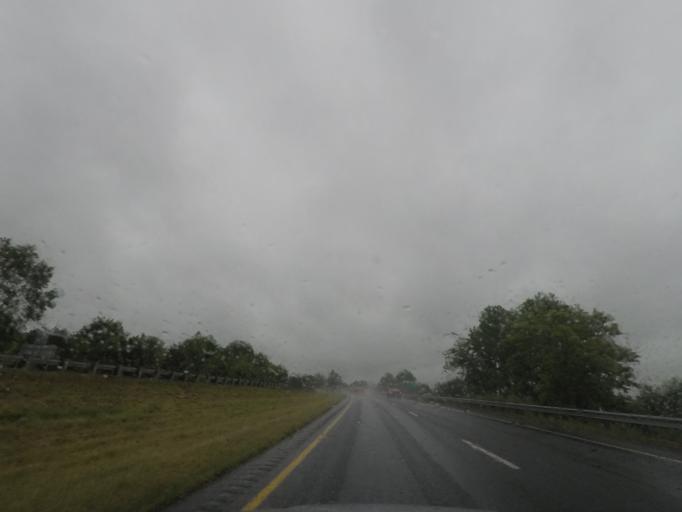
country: US
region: Virginia
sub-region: Fauquier County
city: Bealeton
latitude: 38.5254
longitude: -77.8244
